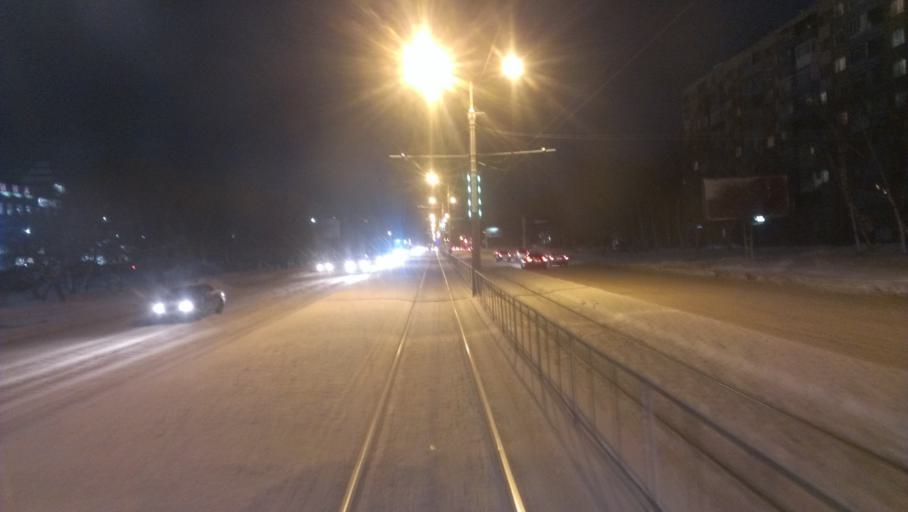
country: RU
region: Altai Krai
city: Novosilikatnyy
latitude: 53.3676
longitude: 83.6766
